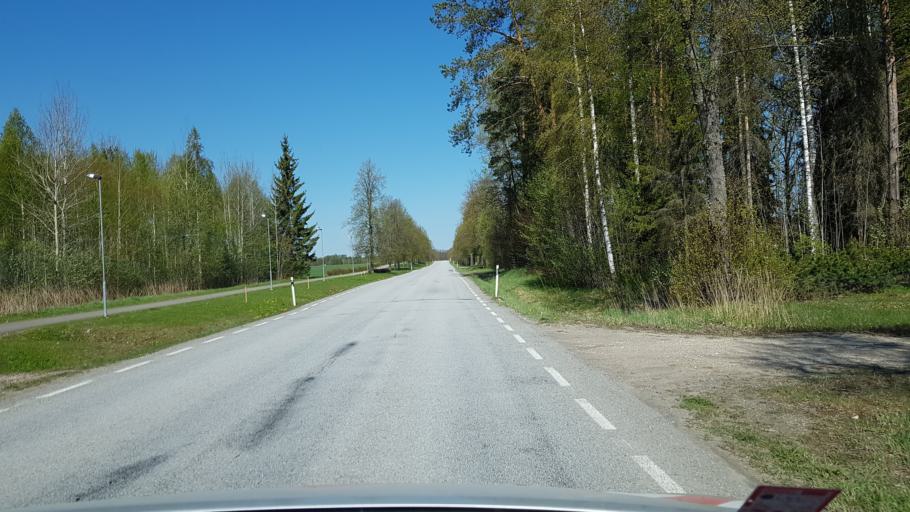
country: EE
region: Vorumaa
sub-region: Voru linn
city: Voru
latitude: 57.8923
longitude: 27.0022
